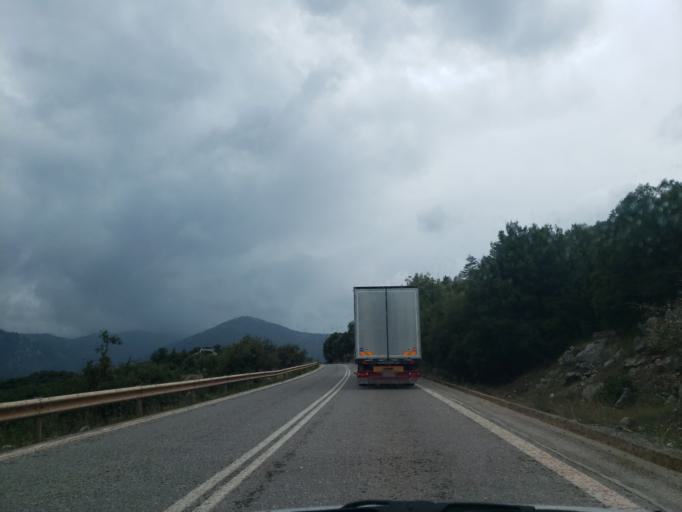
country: GR
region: Central Greece
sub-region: Nomos Fokidos
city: Amfissa
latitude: 38.6430
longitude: 22.3976
